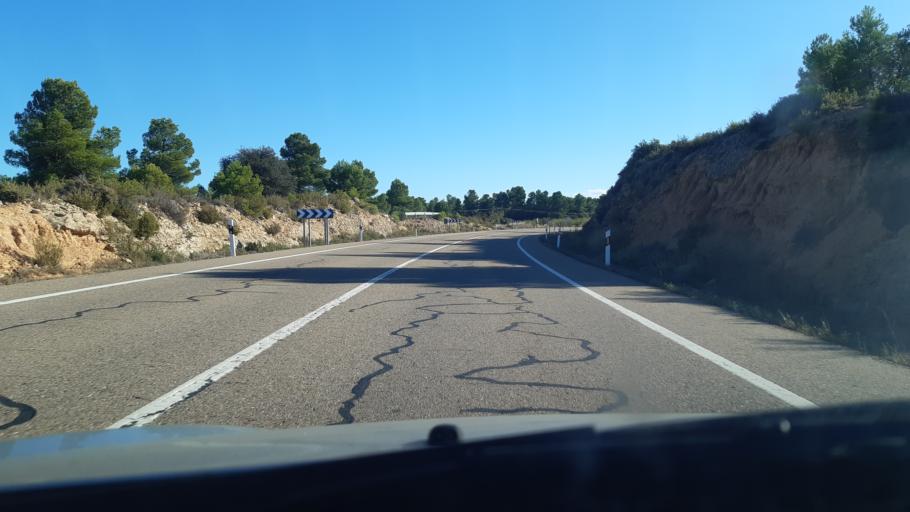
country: ES
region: Aragon
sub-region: Provincia de Teruel
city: Valjunquera
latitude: 40.9504
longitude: -0.0109
